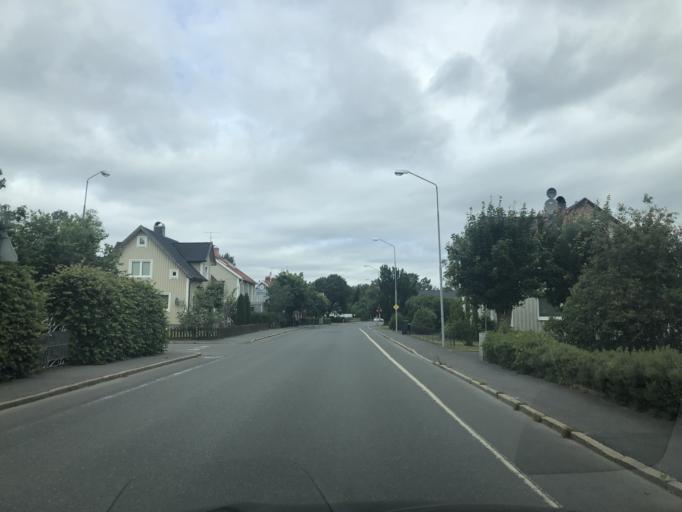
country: SE
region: Joenkoeping
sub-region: Vaggeryds Kommun
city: Vaggeryd
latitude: 57.5014
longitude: 14.1456
